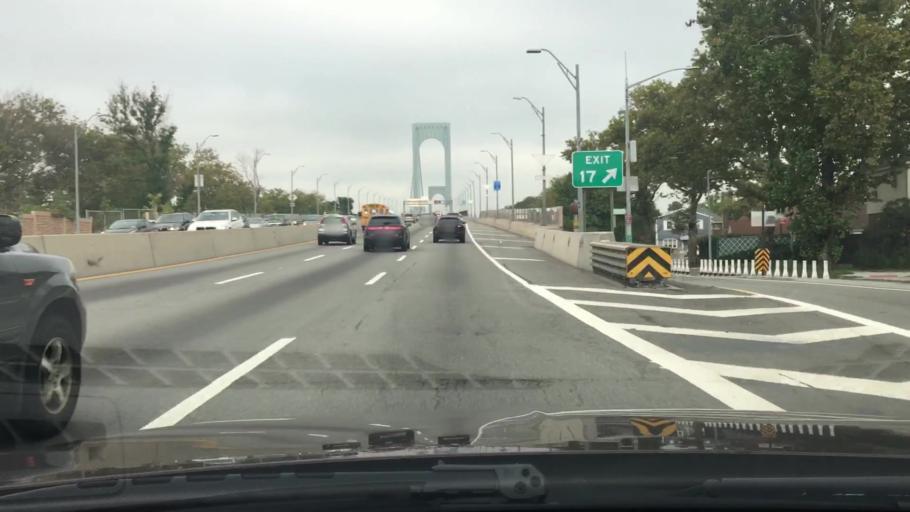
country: US
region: New York
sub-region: Bronx
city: The Bronx
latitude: 40.7934
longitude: -73.8240
